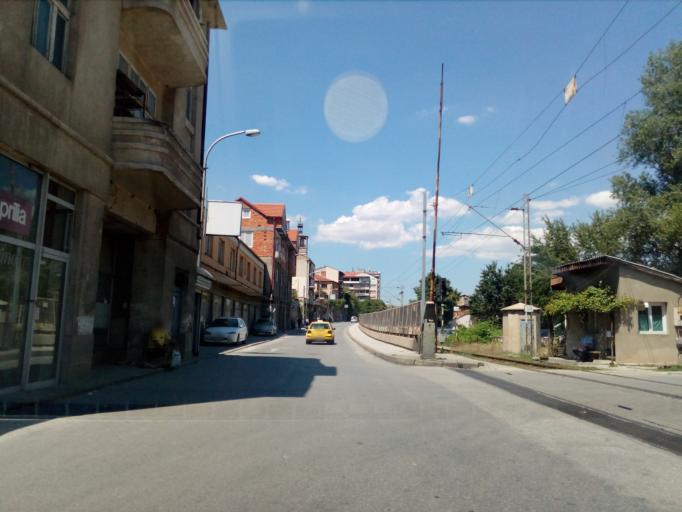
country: MK
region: Veles
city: Veles
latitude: 41.7122
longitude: 21.7844
